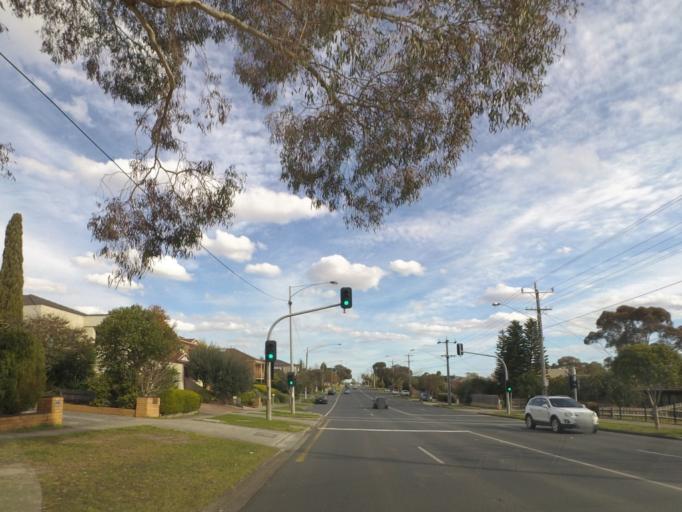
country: AU
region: Victoria
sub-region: Manningham
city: Doncaster East
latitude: -37.7906
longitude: 145.1432
